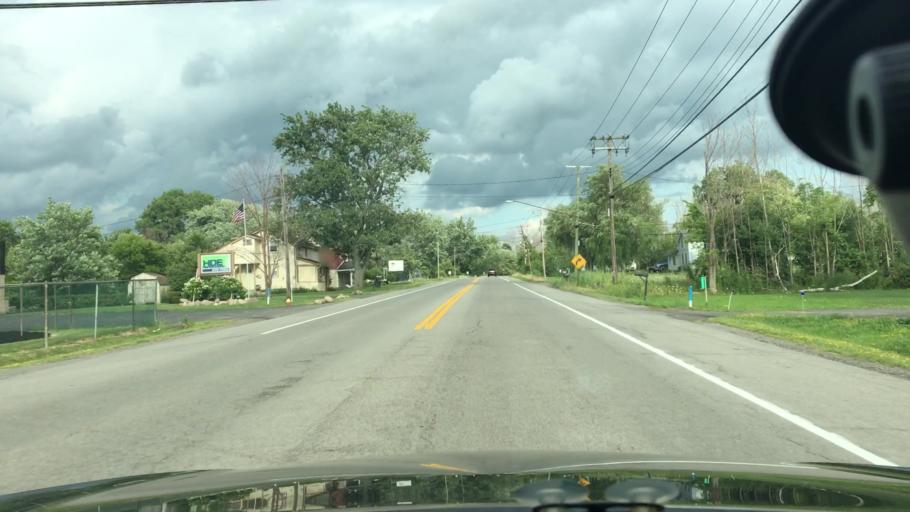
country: US
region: New York
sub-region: Erie County
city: Elma Center
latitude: 42.8264
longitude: -78.6923
